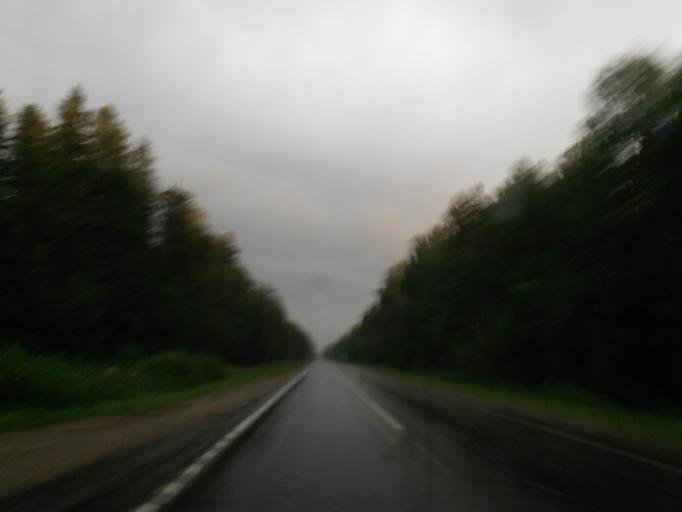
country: RU
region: Jaroslavl
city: Gavrilov-Yam
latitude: 57.4307
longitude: 39.9183
